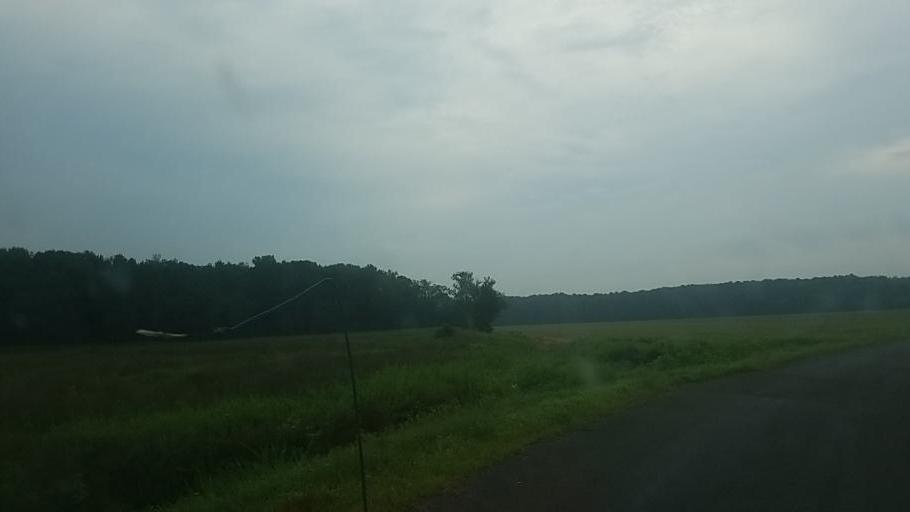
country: US
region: Delaware
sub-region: Sussex County
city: Selbyville
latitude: 38.4483
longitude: -75.2782
